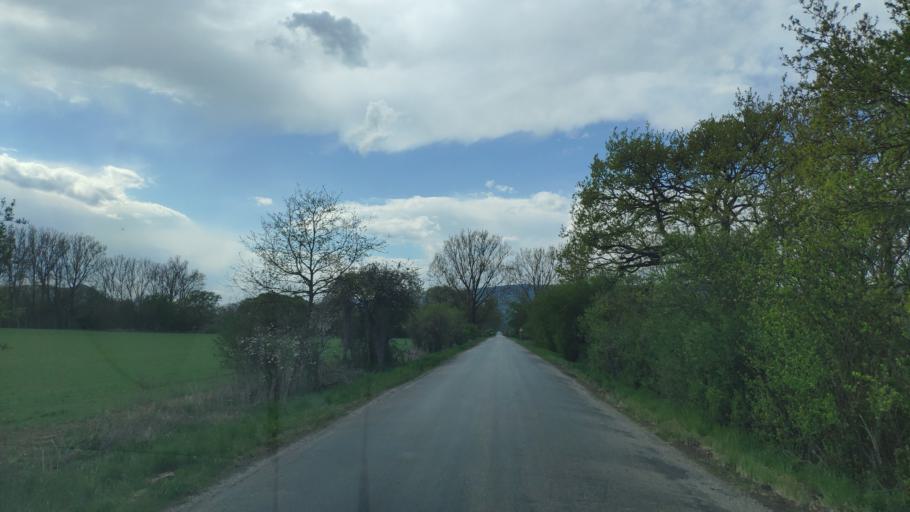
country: SK
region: Kosicky
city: Moldava nad Bodvou
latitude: 48.5909
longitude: 20.9048
